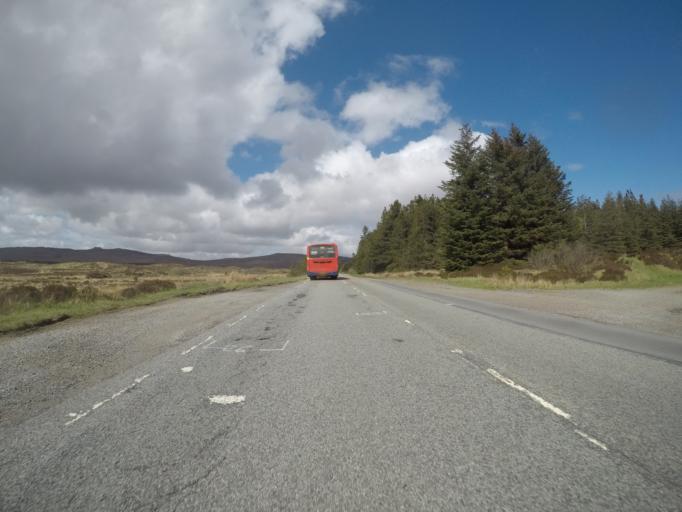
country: GB
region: Scotland
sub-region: Highland
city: Isle of Skye
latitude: 57.3118
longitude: -6.1958
